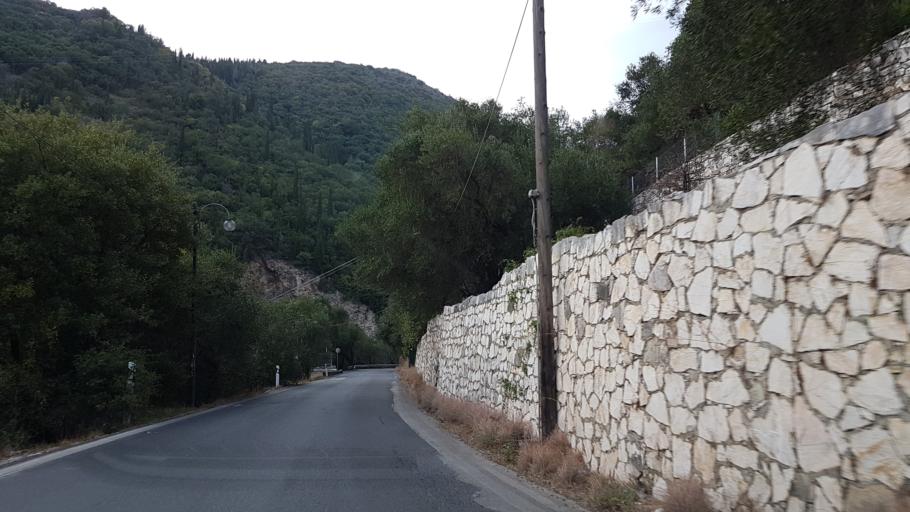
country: GR
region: Ionian Islands
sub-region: Nomos Kerkyras
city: Kontokali
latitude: 39.7340
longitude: 19.9210
